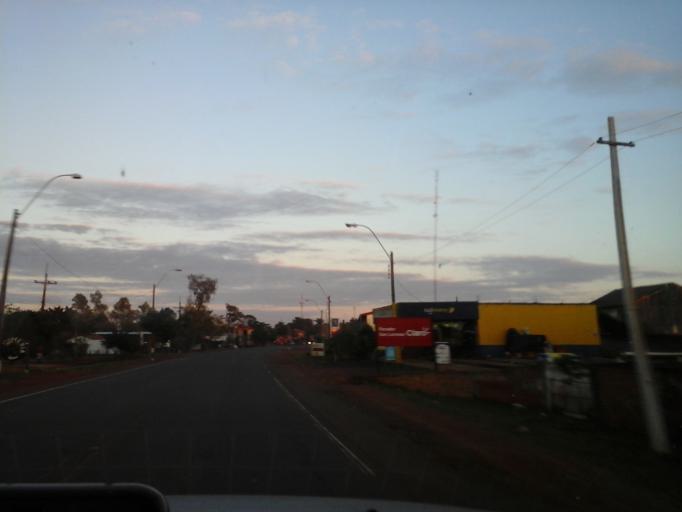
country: PY
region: Itapua
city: General Delgado
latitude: -27.0903
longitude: -56.5184
